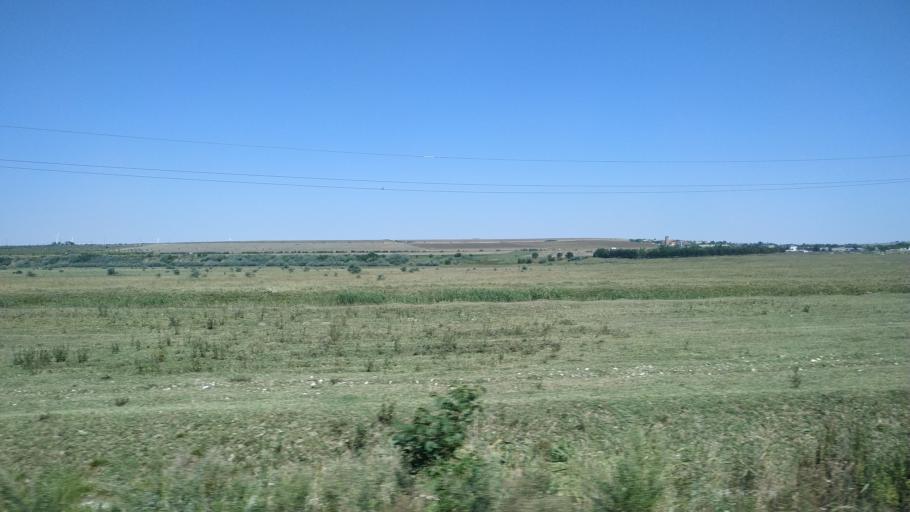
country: RO
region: Constanta
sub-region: Comuna Mircea Voda
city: Satu Nou
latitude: 44.2604
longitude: 28.2088
